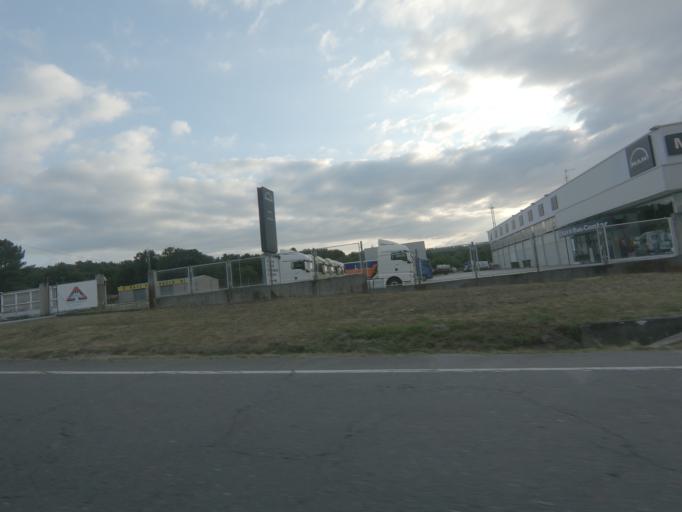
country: ES
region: Galicia
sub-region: Provincia de Ourense
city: Taboadela
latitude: 42.2784
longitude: -7.8365
